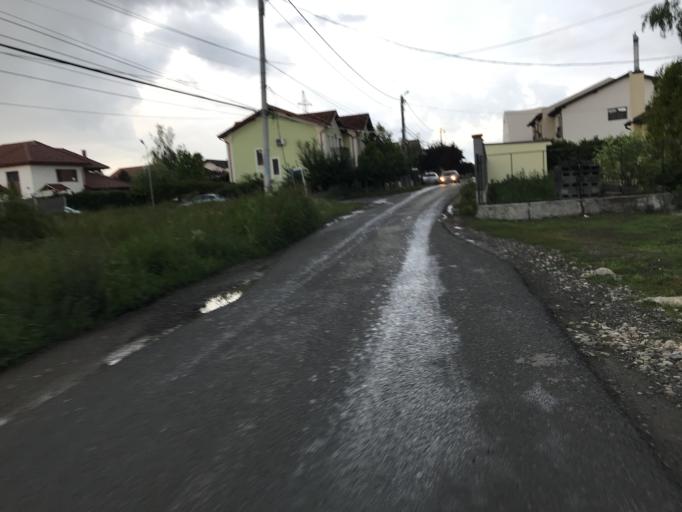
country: RO
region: Timis
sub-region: Comuna Dumbravita
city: Dumbravita
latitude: 45.7875
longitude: 21.2328
